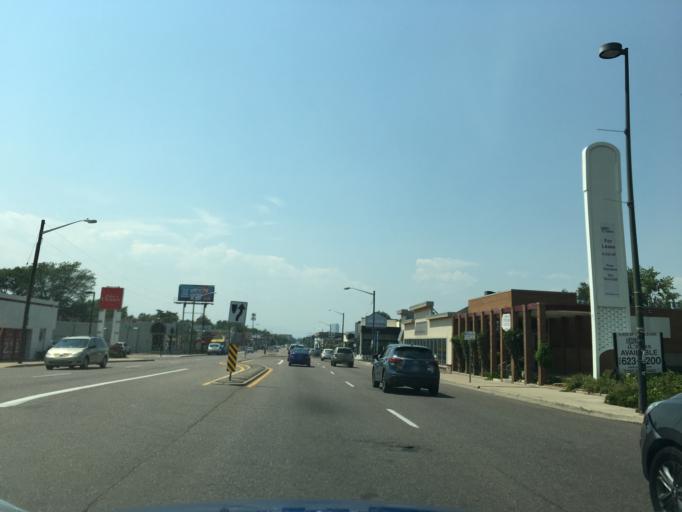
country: US
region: Colorado
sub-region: Arapahoe County
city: Glendale
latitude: 39.7402
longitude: -104.9172
